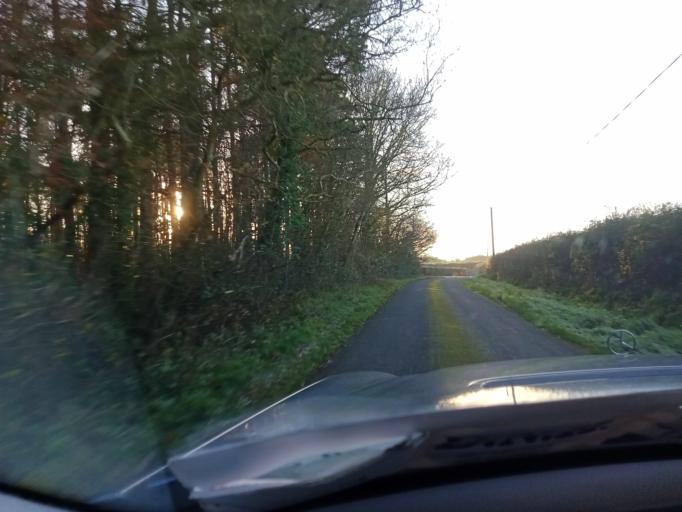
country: IE
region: Leinster
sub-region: Kilkenny
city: Callan
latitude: 52.5330
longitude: -7.4286
